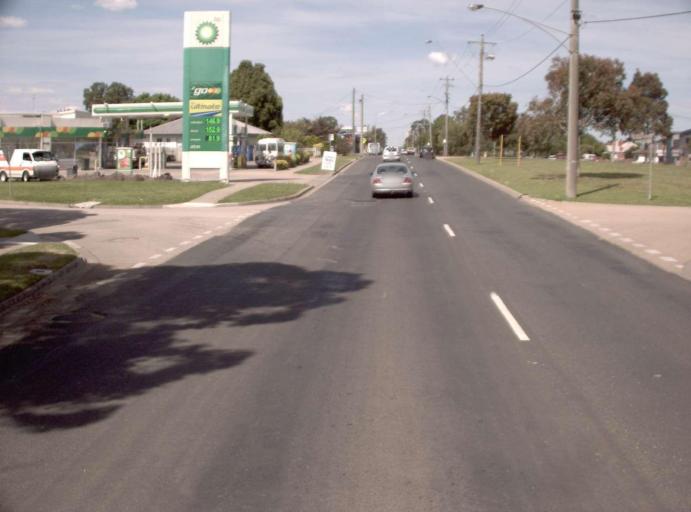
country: AU
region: Victoria
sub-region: East Gippsland
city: Bairnsdale
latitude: -37.8295
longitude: 147.6141
